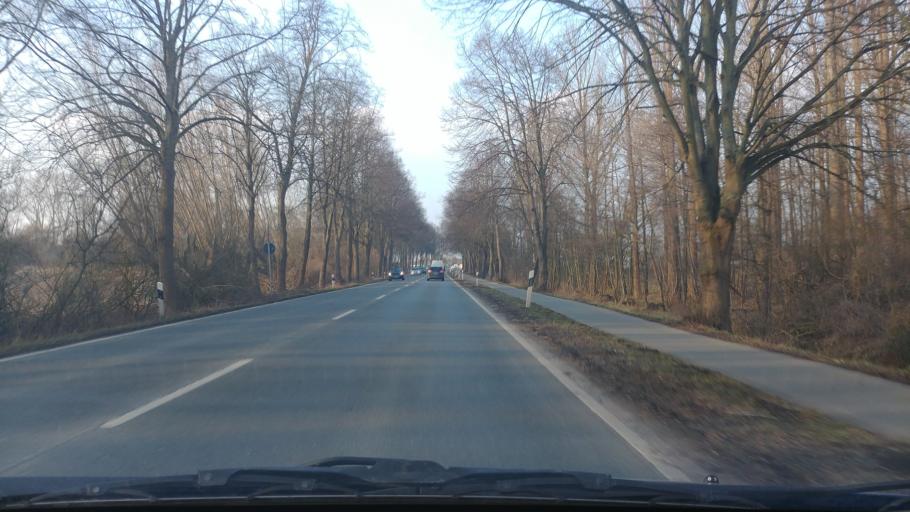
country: DE
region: Lower Saxony
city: Hemmingen
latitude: 52.3119
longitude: 9.7320
